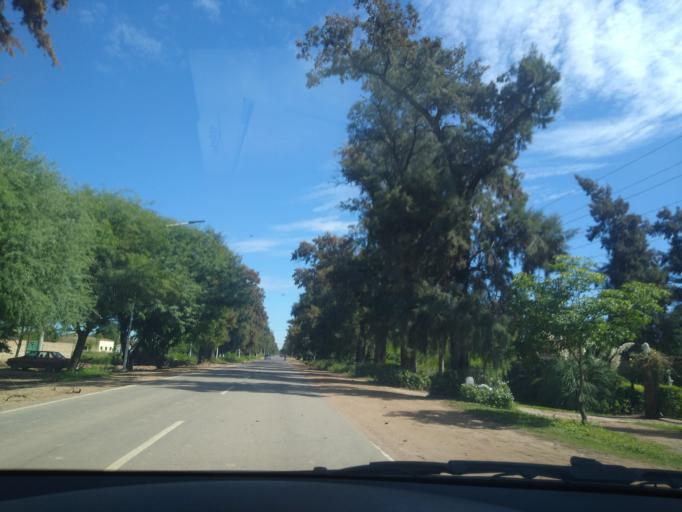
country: AR
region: Chaco
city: Presidencia Roque Saenz Pena
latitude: -26.7738
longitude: -60.4158
